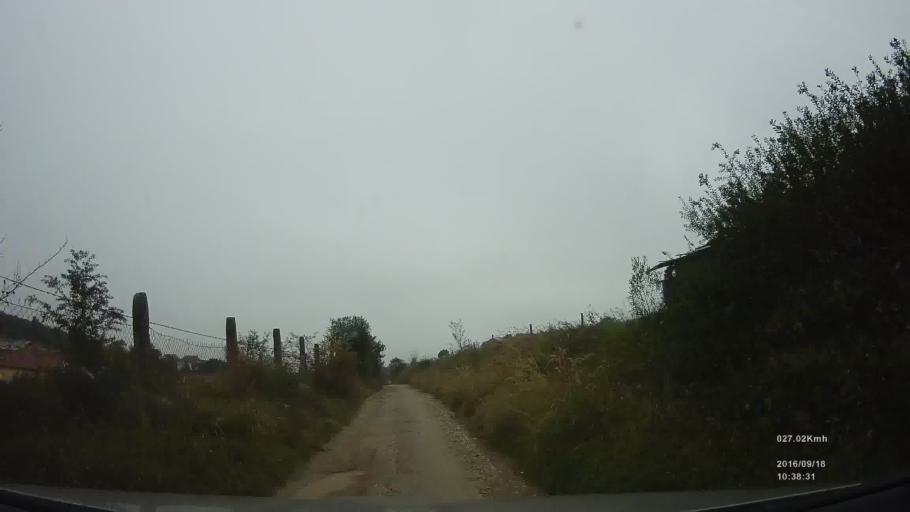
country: SK
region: Kosicky
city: Spisska Nova Ves
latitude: 48.9531
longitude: 20.6214
